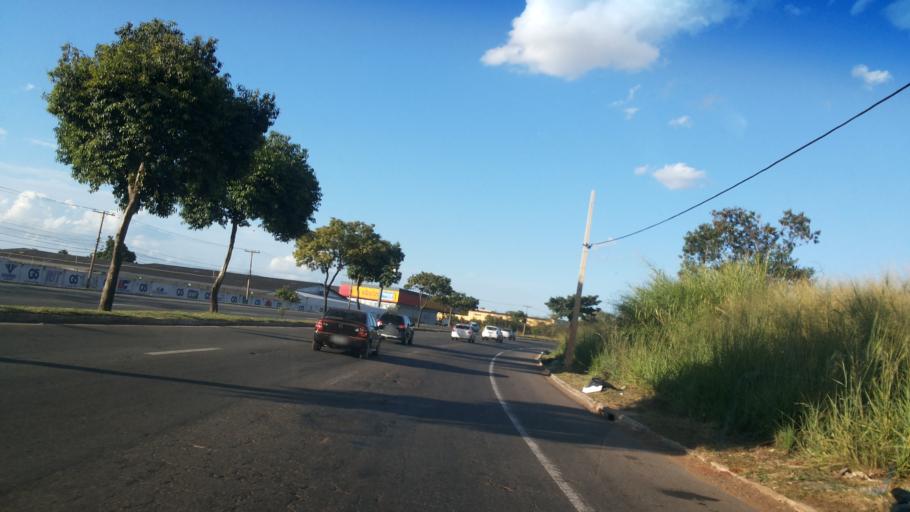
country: BR
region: Goias
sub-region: Goiania
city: Goiania
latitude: -16.6424
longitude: -49.3048
